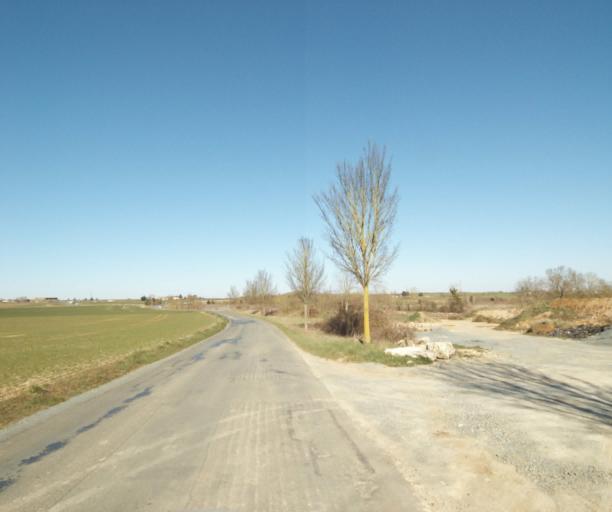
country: FR
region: Poitou-Charentes
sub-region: Departement des Deux-Sevres
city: Bessines
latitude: 46.3410
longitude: -0.5124
